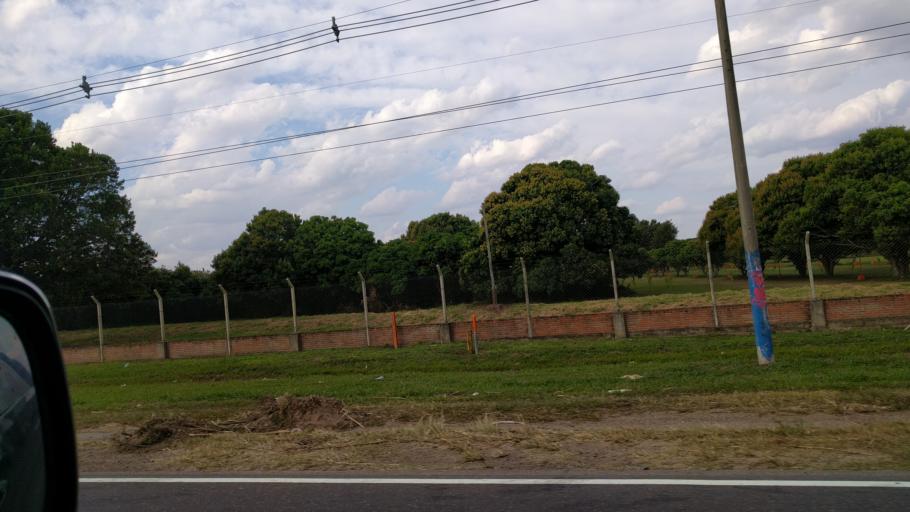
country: BO
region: Santa Cruz
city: Warnes
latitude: -17.5560
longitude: -63.1597
